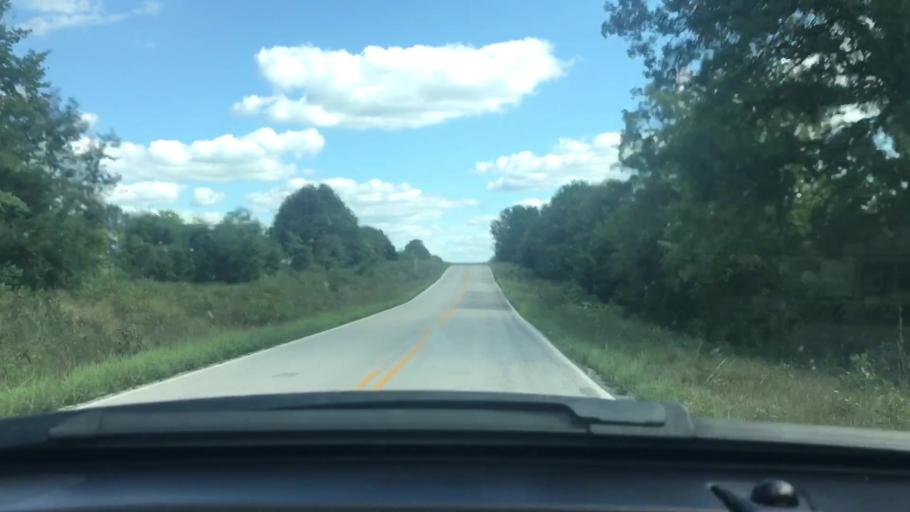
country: US
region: Missouri
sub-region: Wright County
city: Hartville
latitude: 37.3902
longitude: -92.4481
